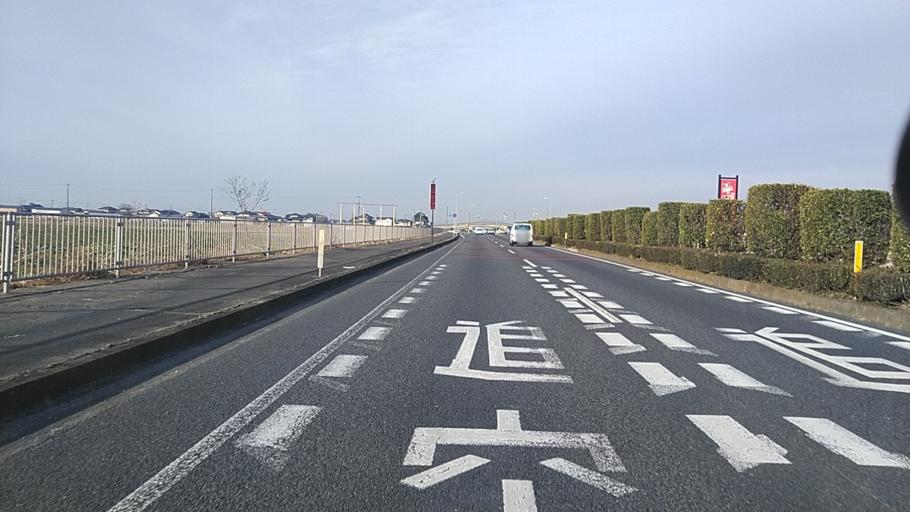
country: JP
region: Tochigi
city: Oyama
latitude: 36.3092
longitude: 139.7562
